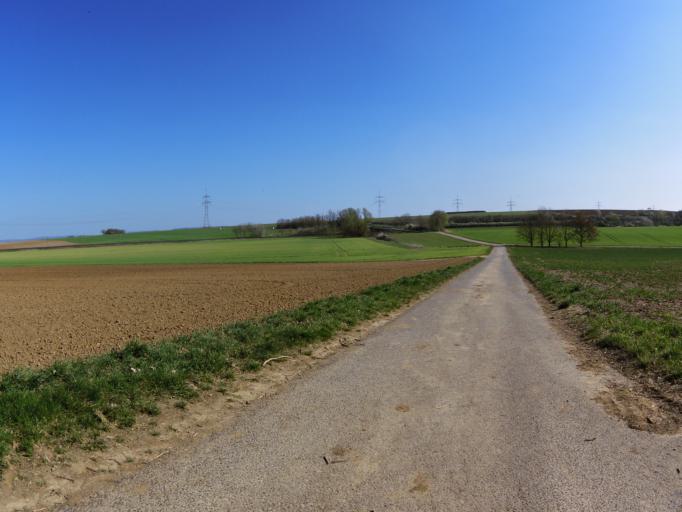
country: DE
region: Bavaria
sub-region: Regierungsbezirk Unterfranken
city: Kurnach
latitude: 49.8296
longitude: 10.0768
